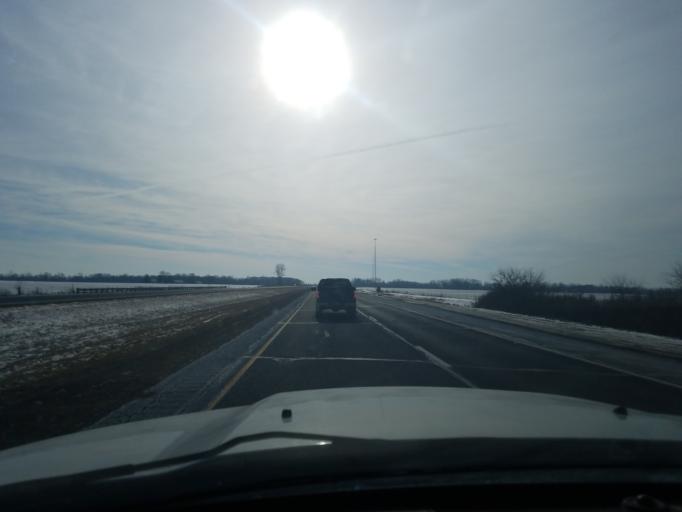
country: US
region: Indiana
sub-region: Huntington County
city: Roanoke
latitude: 40.9121
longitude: -85.3295
